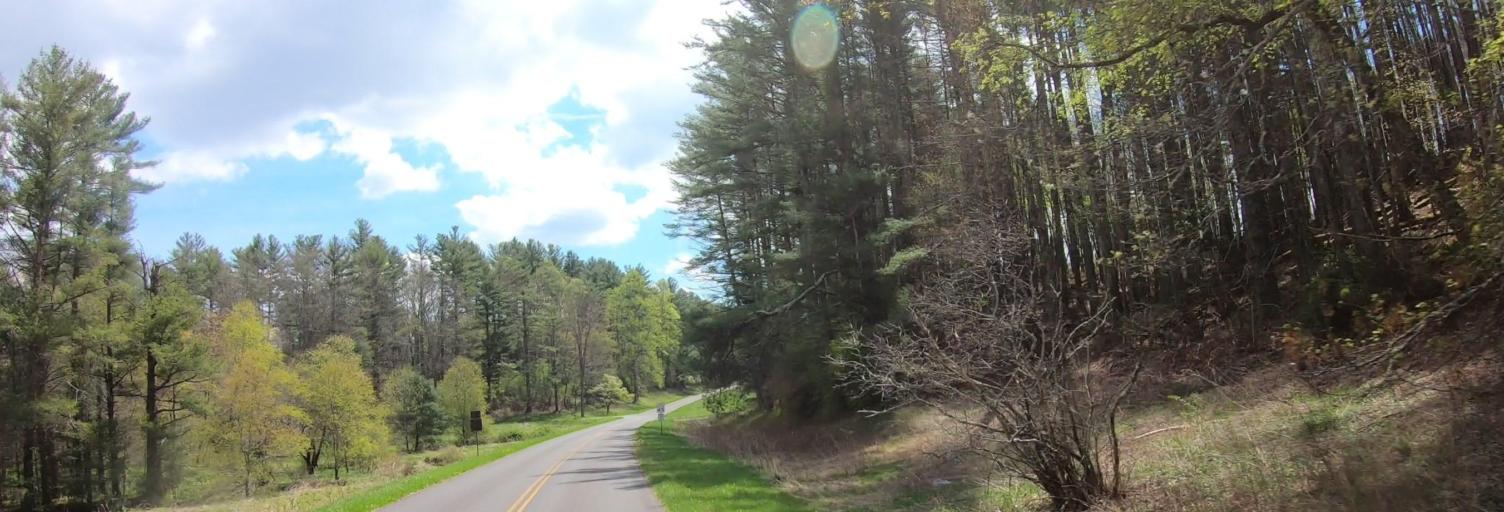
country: US
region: Virginia
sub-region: City of Galax
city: Galax
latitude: 36.5742
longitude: -80.8949
